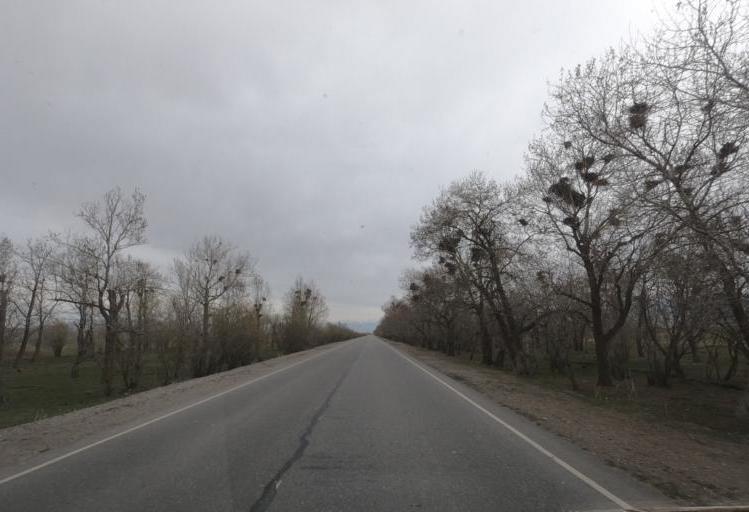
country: KG
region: Naryn
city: At-Bashi
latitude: 41.0854
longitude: 75.5655
